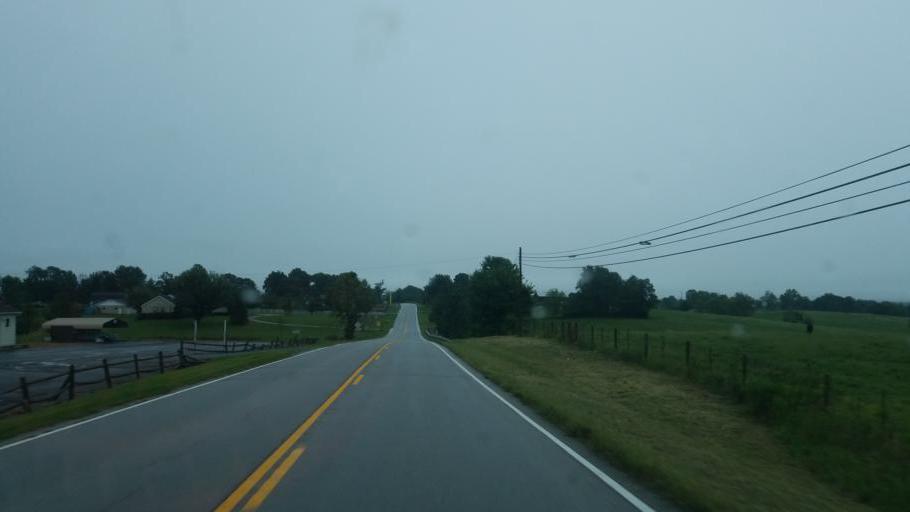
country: US
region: Kentucky
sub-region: Fleming County
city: Flemingsburg
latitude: 38.3923
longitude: -83.6895
